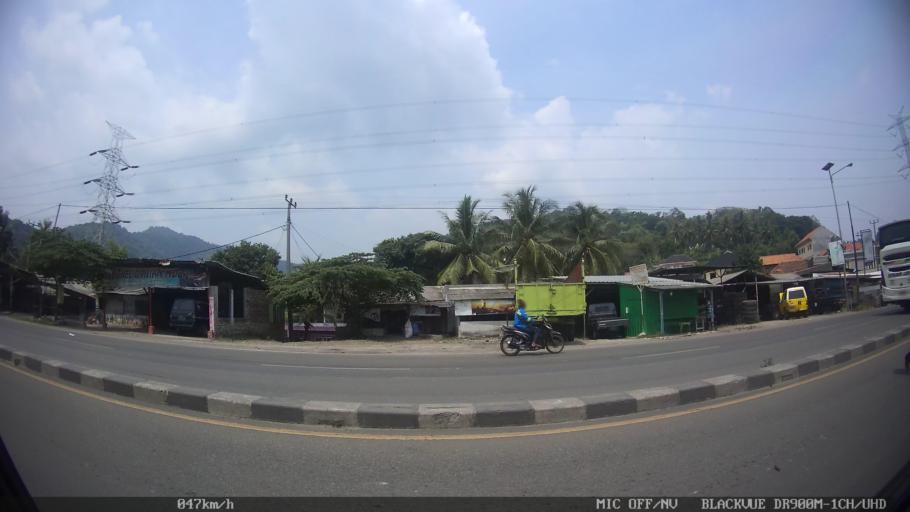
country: ID
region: Banten
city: Curug
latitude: -5.9620
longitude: 106.0065
